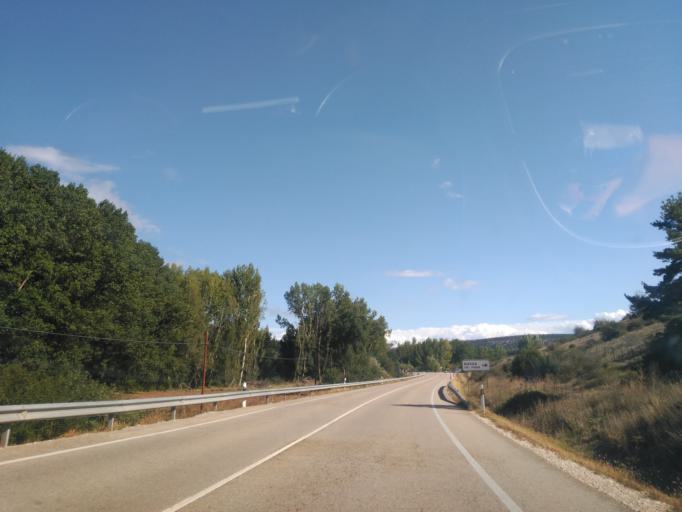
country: ES
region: Castille and Leon
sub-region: Provincia de Burgos
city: Rabanera del Pinar
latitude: 41.8609
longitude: -3.1989
